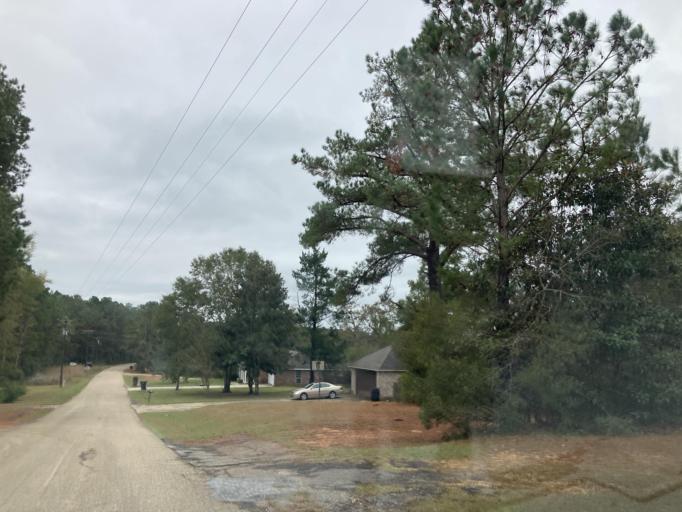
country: US
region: Mississippi
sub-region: Lamar County
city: West Hattiesburg
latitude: 31.2622
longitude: -89.5058
